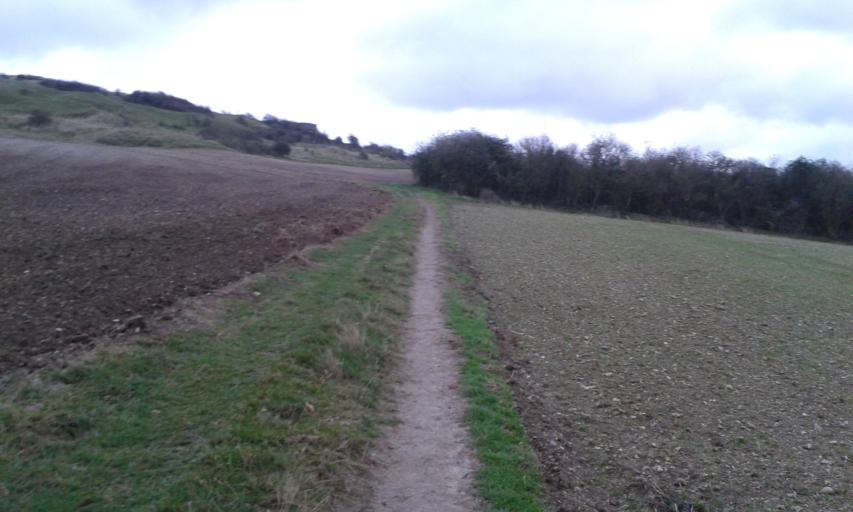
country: FR
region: Nord-Pas-de-Calais
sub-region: Departement du Pas-de-Calais
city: Wissant
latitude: 50.8724
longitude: 1.7018
